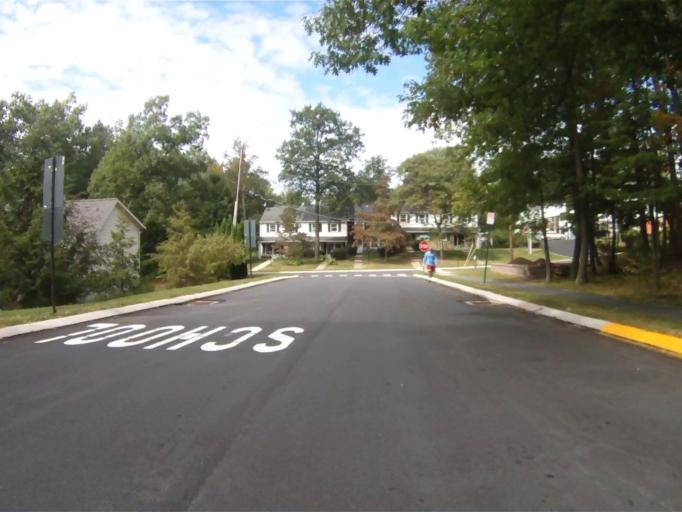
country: US
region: Pennsylvania
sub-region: Centre County
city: Park Forest Village
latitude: 40.8077
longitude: -77.9226
